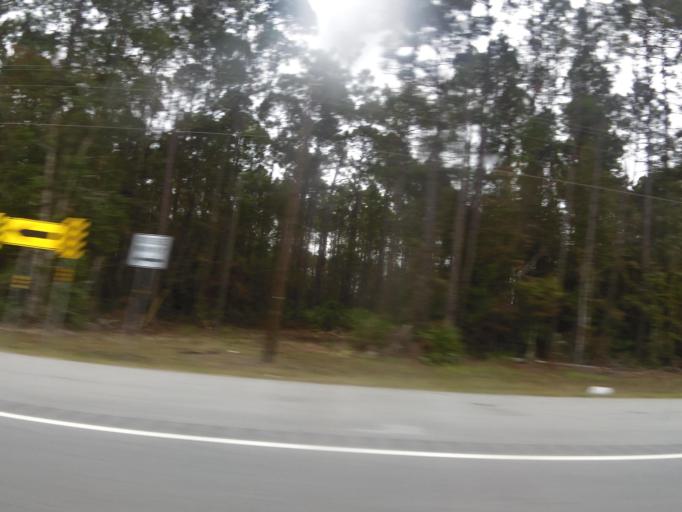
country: US
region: Georgia
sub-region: Charlton County
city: Folkston
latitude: 30.8737
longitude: -82.0233
